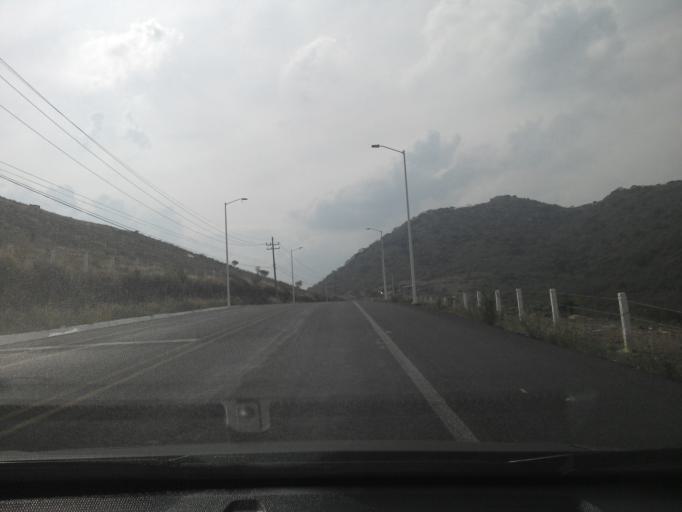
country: MX
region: Jalisco
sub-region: Tlajomulco de Zuniga
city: Lomas del Sur
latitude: 20.4878
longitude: -103.4226
